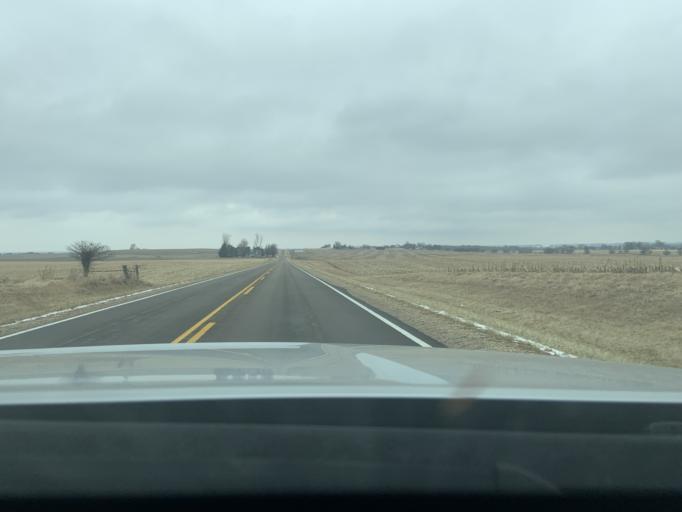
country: US
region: Illinois
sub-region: LaSalle County
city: Sheridan
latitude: 41.4603
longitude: -88.6154
